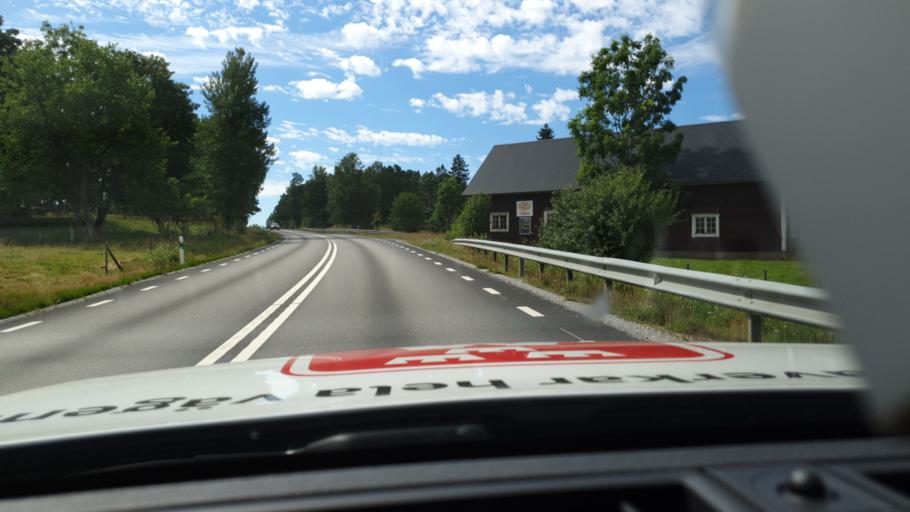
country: SE
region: Joenkoeping
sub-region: Savsjo Kommun
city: Stockaryd
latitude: 57.2546
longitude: 14.5181
